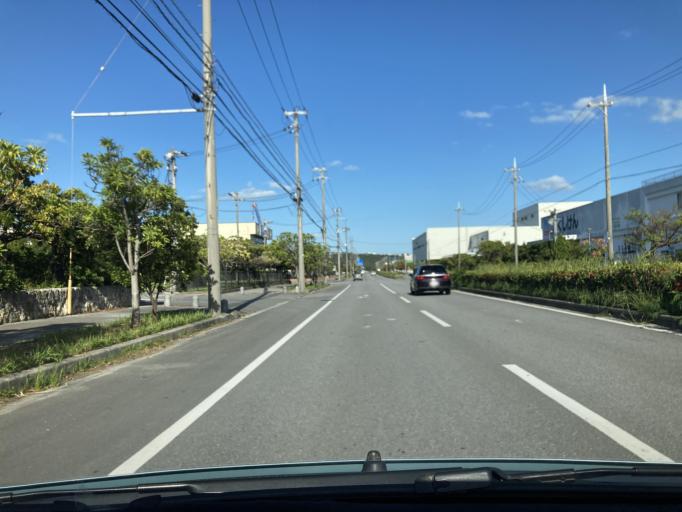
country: JP
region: Okinawa
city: Katsuren-haebaru
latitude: 26.3366
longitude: 127.8513
